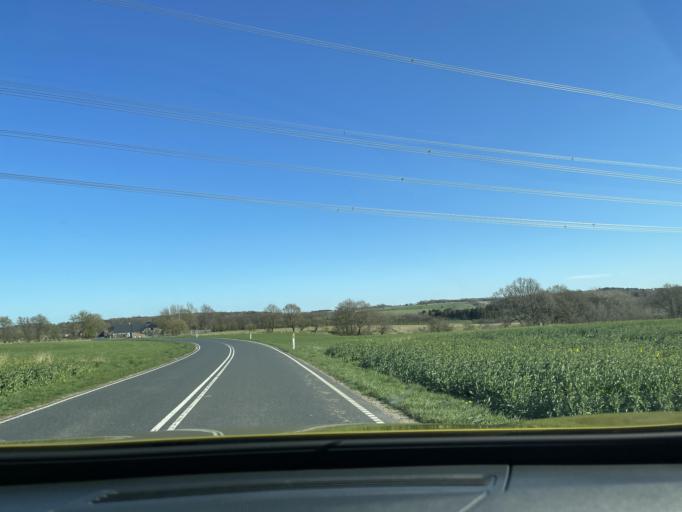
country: DK
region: Central Jutland
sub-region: Silkeborg Kommune
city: Kjellerup
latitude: 56.2509
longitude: 9.4454
